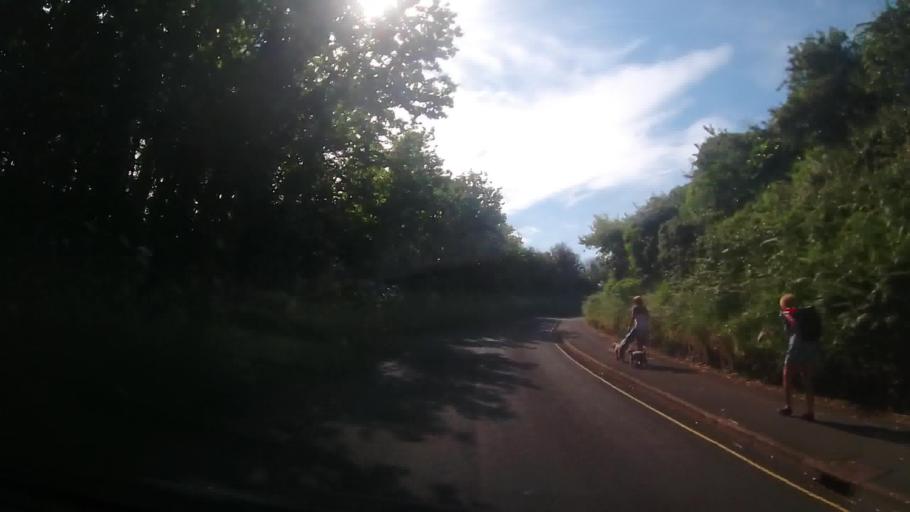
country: GB
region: England
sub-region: Devon
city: Dartmouth
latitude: 50.2879
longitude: -3.6473
